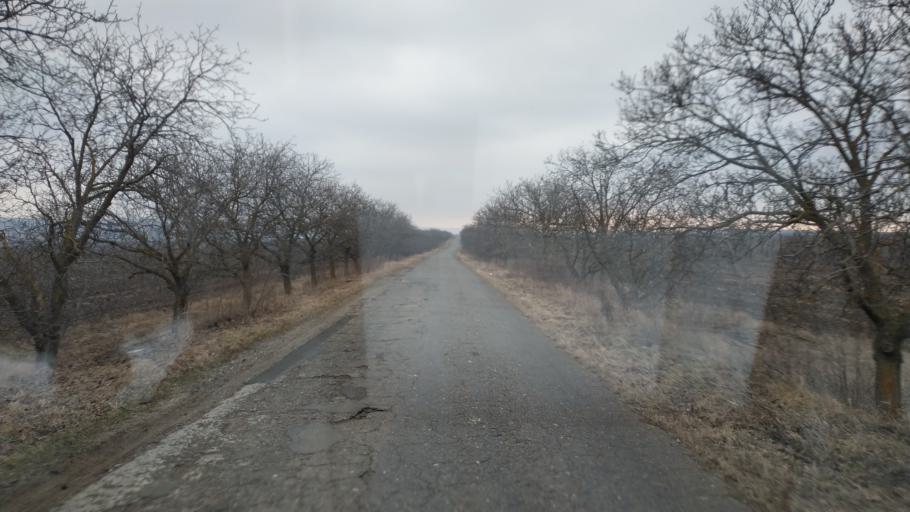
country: MD
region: Hincesti
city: Dancu
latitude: 46.8847
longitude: 28.2999
